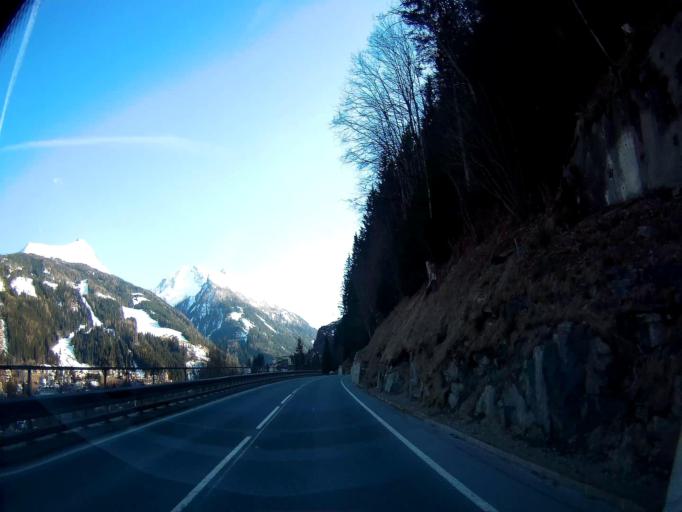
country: AT
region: Salzburg
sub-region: Politischer Bezirk Sankt Johann im Pongau
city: Bad Gastein
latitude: 47.1263
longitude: 13.1310
